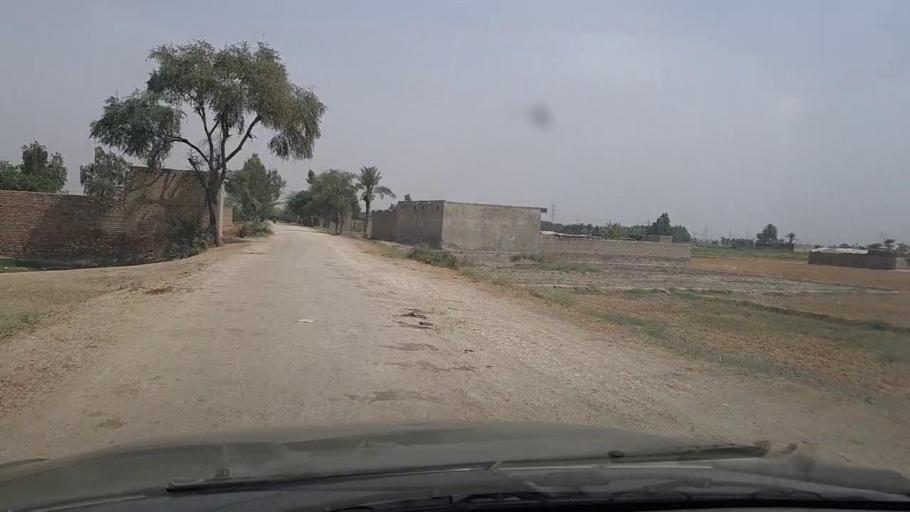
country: PK
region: Sindh
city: Shikarpur
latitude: 27.9261
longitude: 68.6666
